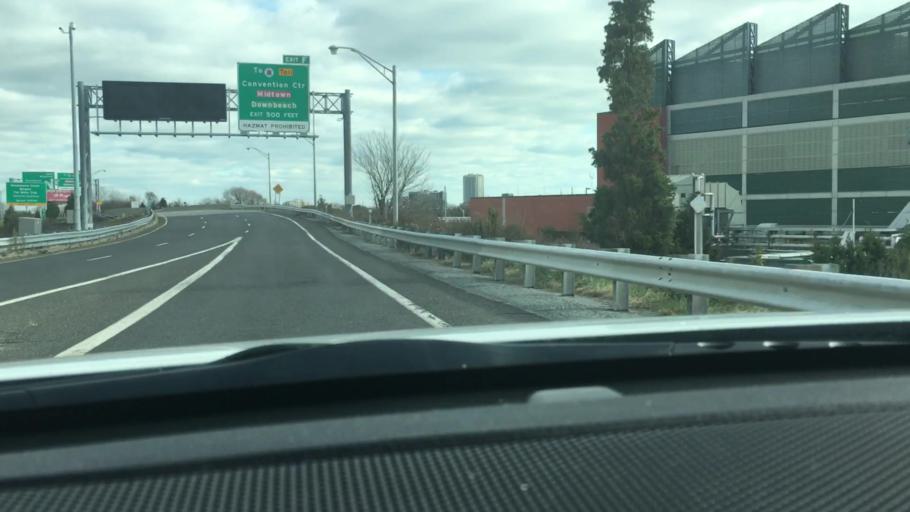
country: US
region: New Jersey
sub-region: Atlantic County
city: Atlantic City
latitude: 39.3736
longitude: -74.4374
